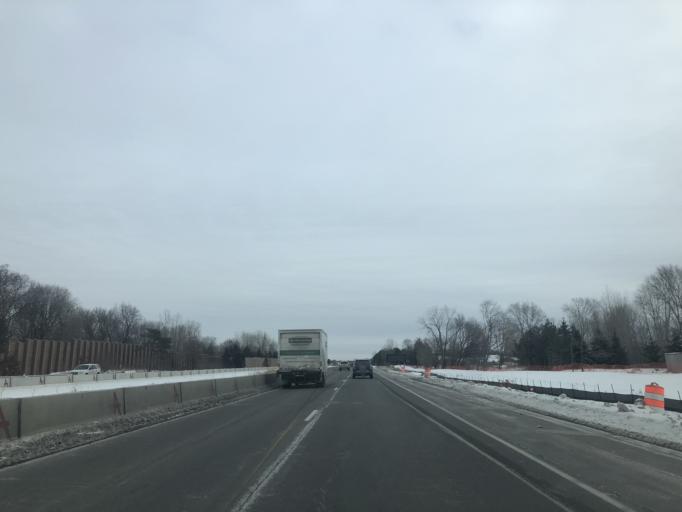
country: US
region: Minnesota
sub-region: Anoka County
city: Circle Pines
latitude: 45.1681
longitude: -93.1426
